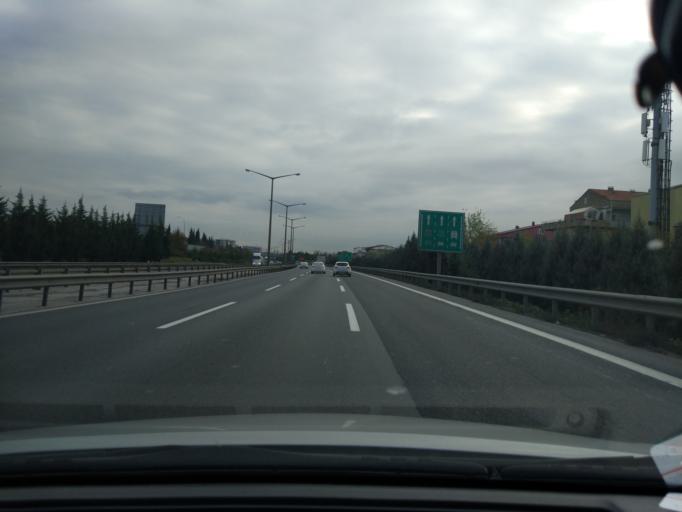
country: TR
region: Kocaeli
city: Korfez
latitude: 40.7708
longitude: 29.7780
